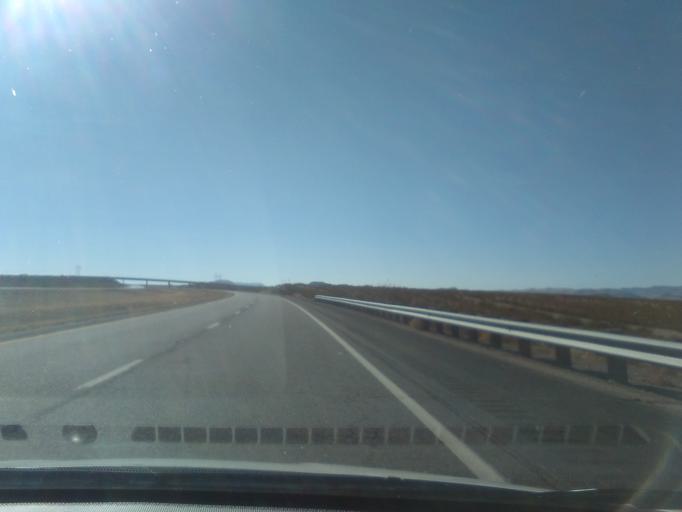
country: US
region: New Mexico
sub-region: Sierra County
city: Elephant Butte
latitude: 33.6122
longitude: -107.1494
